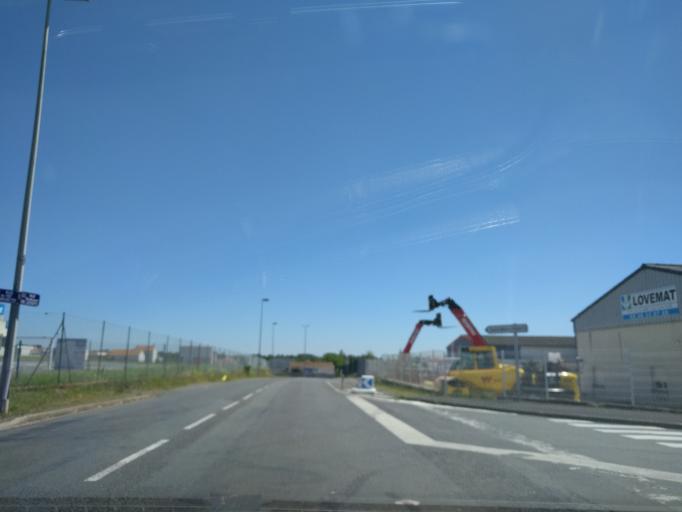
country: FR
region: Poitou-Charentes
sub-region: Departement des Deux-Sevres
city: Aiffres
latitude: 46.3321
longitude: -0.4216
